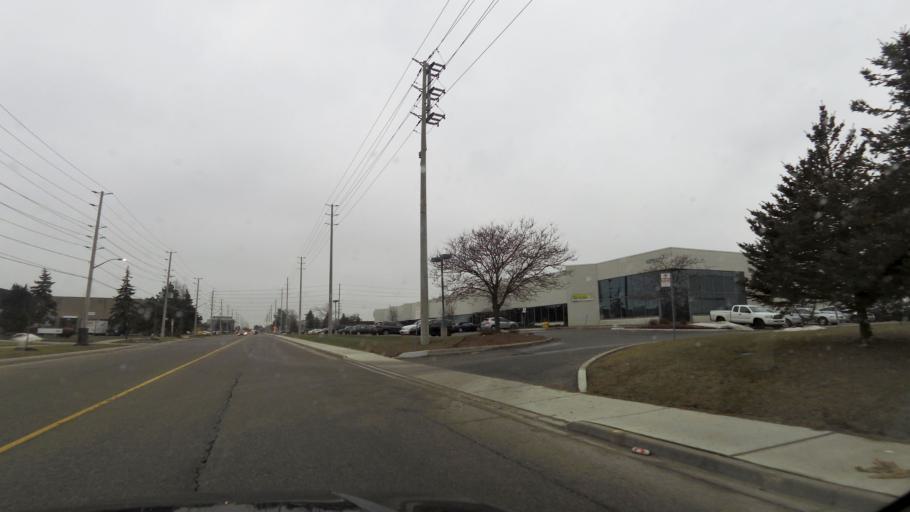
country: CA
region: Ontario
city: Etobicoke
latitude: 43.6962
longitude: -79.6139
